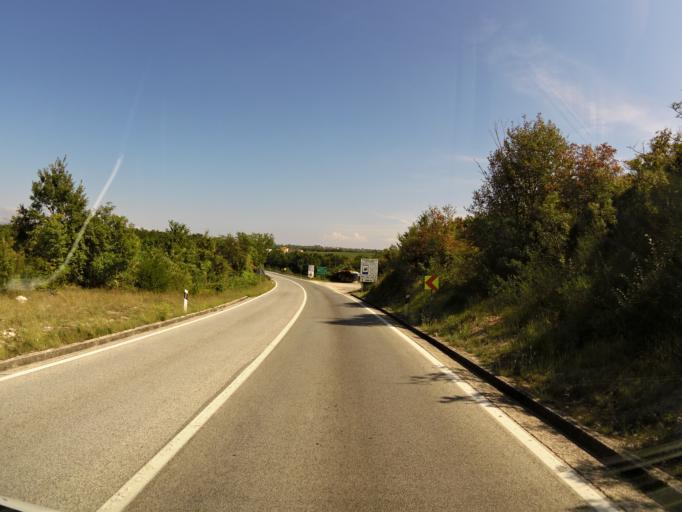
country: HR
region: Zadarska
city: Policnik
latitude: 44.1907
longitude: 15.4122
